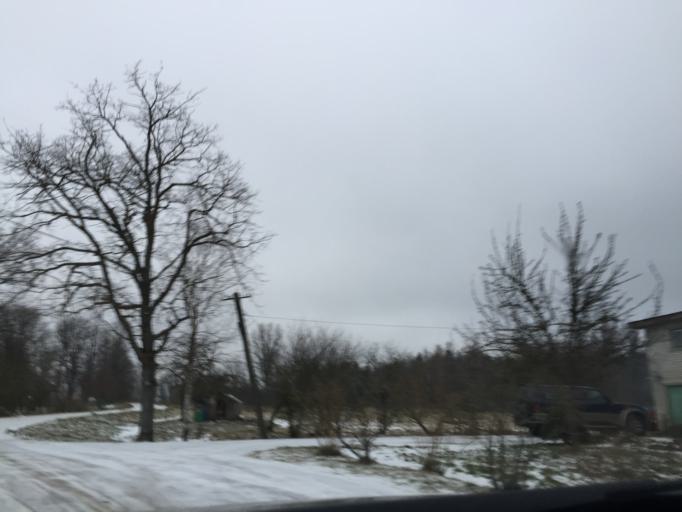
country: LV
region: Saulkrastu
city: Saulkrasti
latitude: 57.5068
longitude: 24.3827
